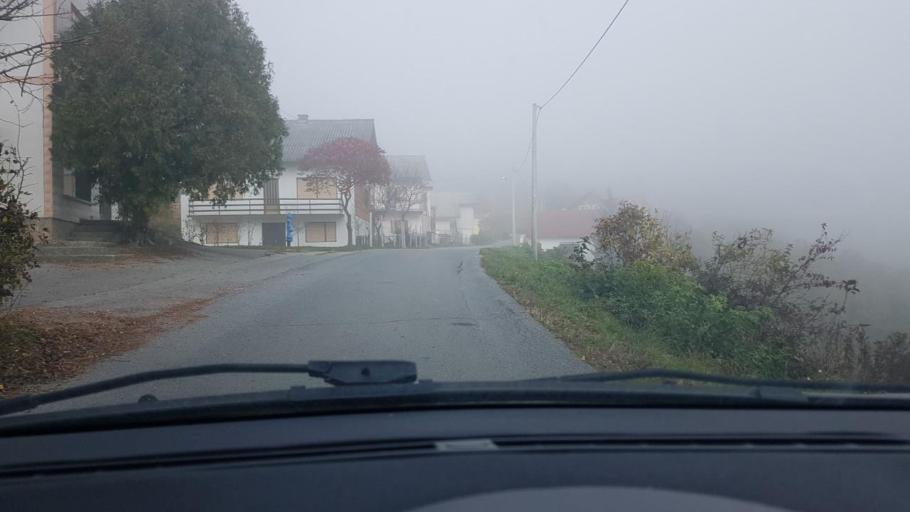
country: HR
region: Krapinsko-Zagorska
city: Mihovljan
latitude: 46.1561
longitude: 15.9895
